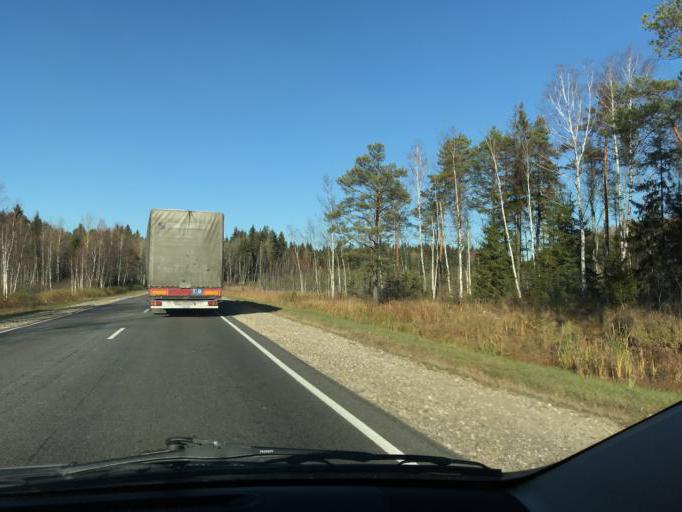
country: BY
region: Vitebsk
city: Polatsk
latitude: 55.5193
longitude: 28.7341
